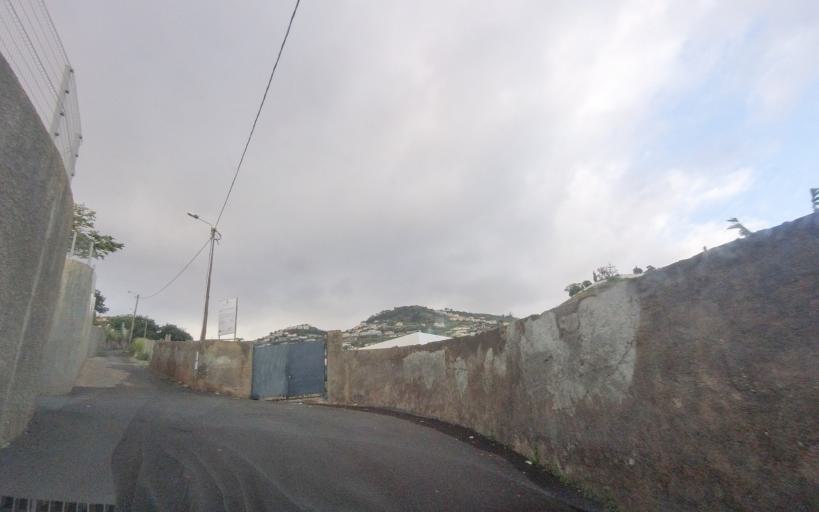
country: PT
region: Madeira
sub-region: Funchal
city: Funchal
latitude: 32.6465
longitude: -16.8834
